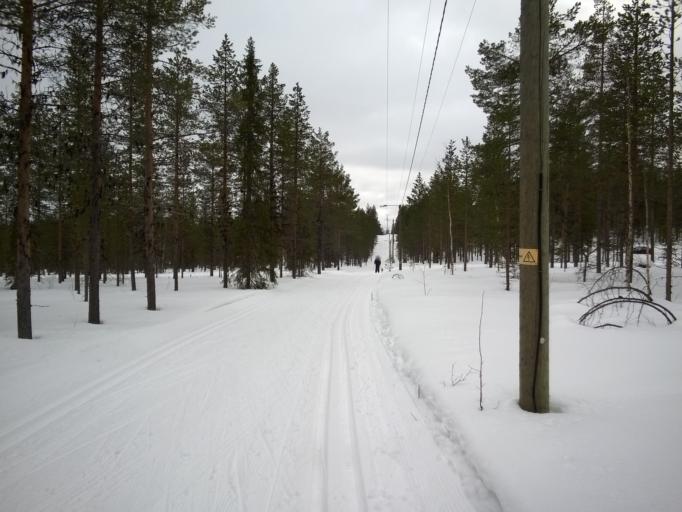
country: FI
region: Lapland
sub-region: Tunturi-Lappi
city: Muonio
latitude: 67.9199
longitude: 23.9335
